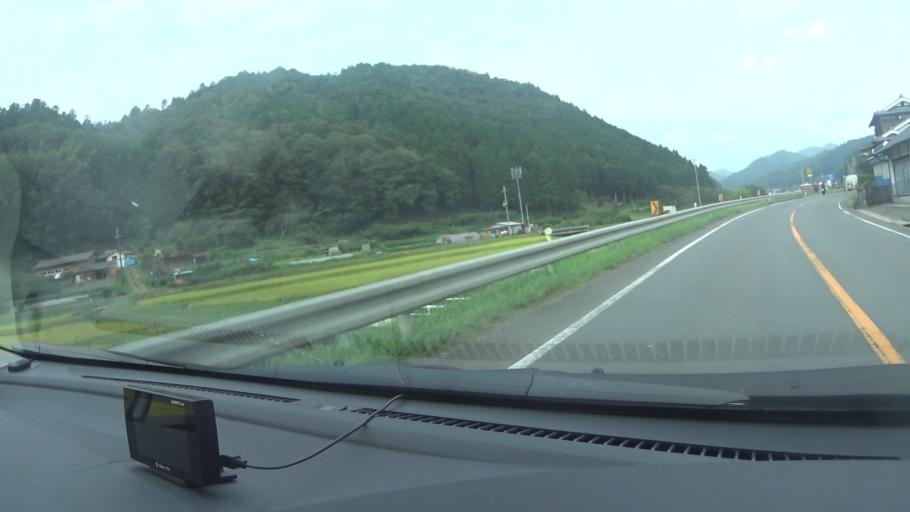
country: JP
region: Kyoto
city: Ayabe
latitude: 35.2063
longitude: 135.3521
